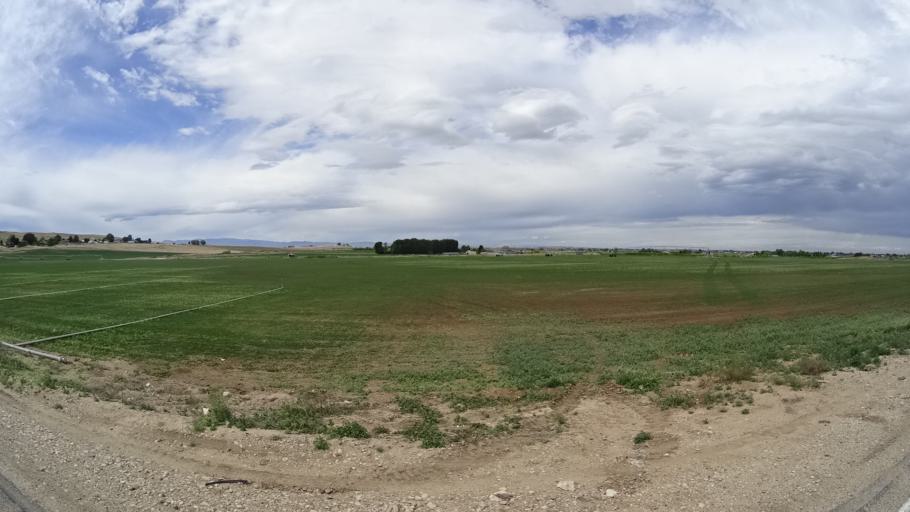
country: US
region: Idaho
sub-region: Ada County
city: Kuna
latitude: 43.4657
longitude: -116.4437
